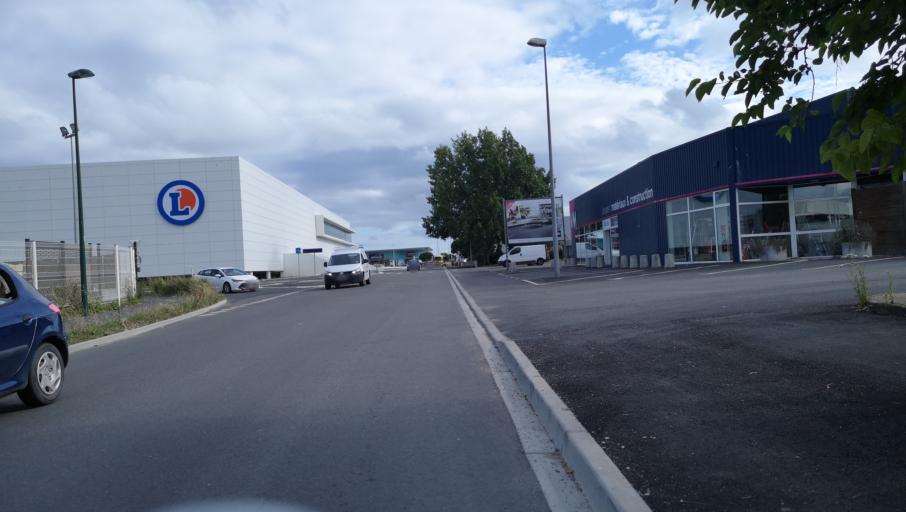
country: FR
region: Pays de la Loire
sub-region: Departement de la Vendee
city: Les Sables-d'Olonne
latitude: 46.5165
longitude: -1.7812
